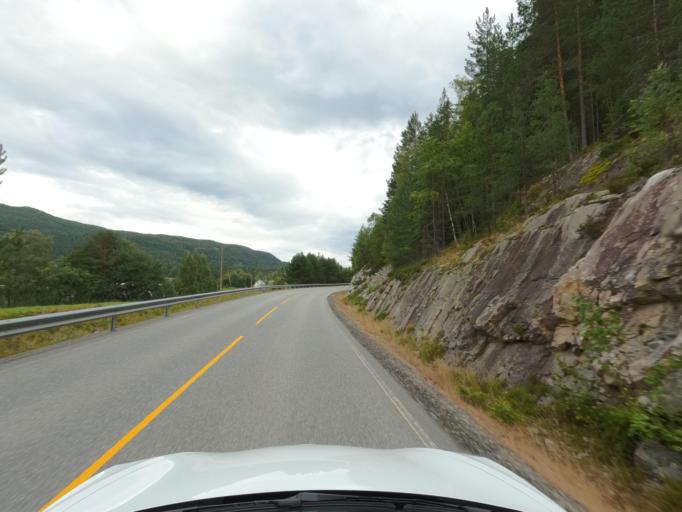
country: NO
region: Telemark
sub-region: Hjartdal
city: Sauland
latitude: 59.7294
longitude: 9.0193
